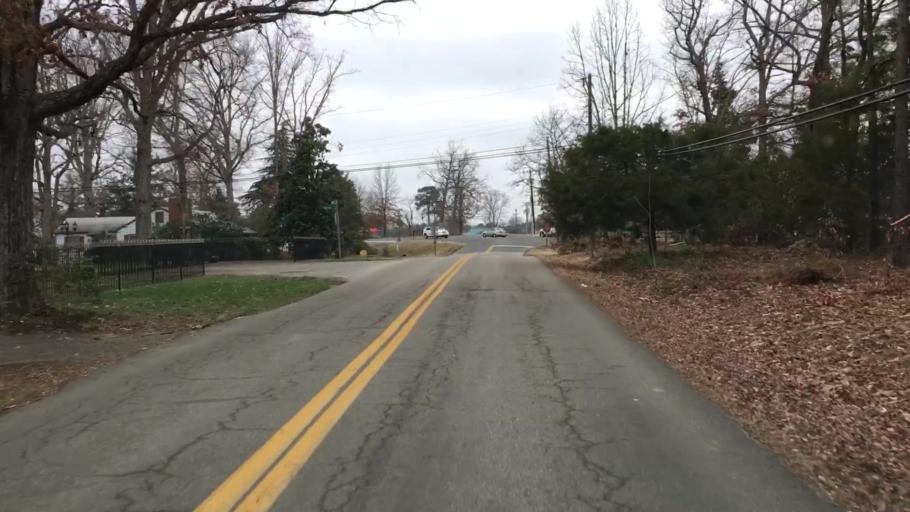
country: US
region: Virginia
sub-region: Chesterfield County
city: Bon Air
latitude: 37.5342
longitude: -77.5628
